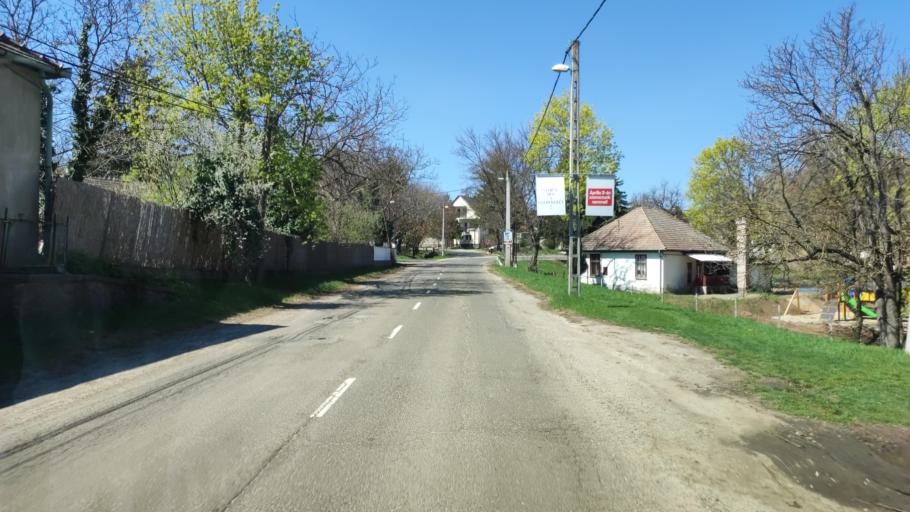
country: HU
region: Pest
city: Kosd
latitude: 47.8003
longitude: 19.1776
